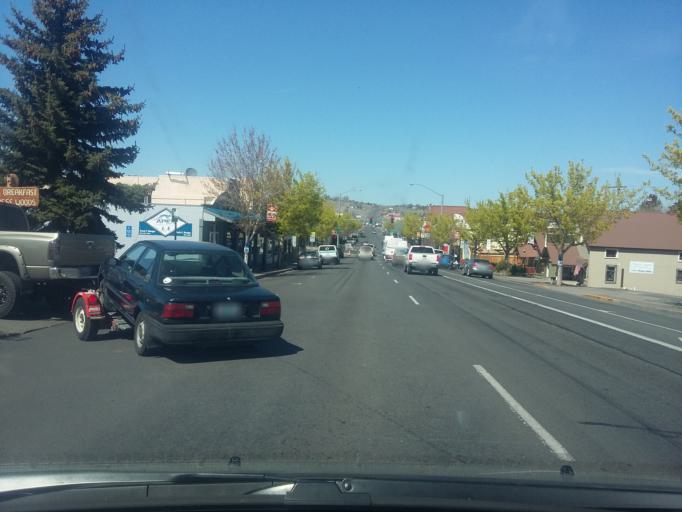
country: US
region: Oregon
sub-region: Jefferson County
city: Madras
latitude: 44.6325
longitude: -121.1296
